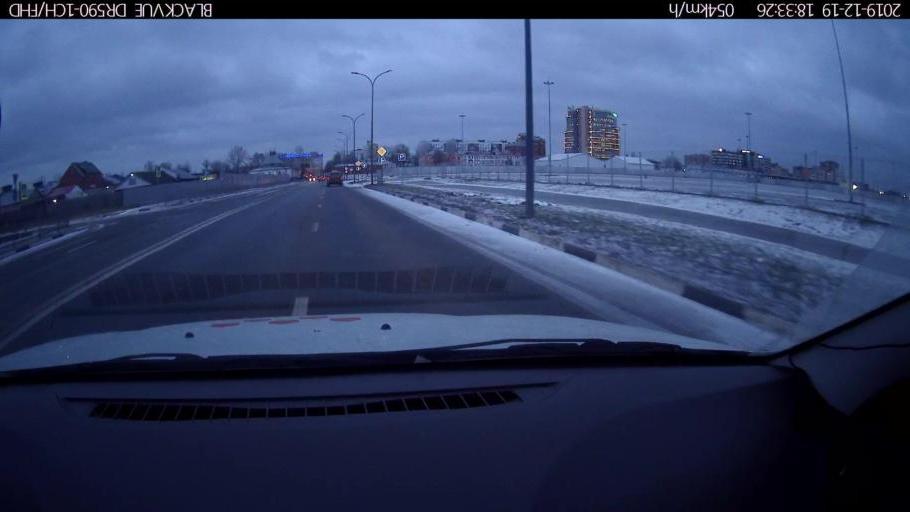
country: RU
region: Nizjnij Novgorod
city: Nizhniy Novgorod
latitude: 56.3341
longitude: 43.9687
